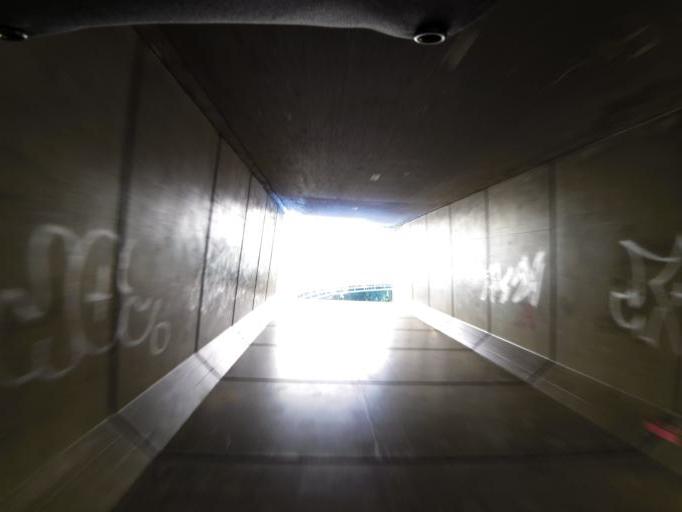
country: NL
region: Overijssel
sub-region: Gemeente Twenterand
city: Den Ham
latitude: 52.5420
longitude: 6.4818
